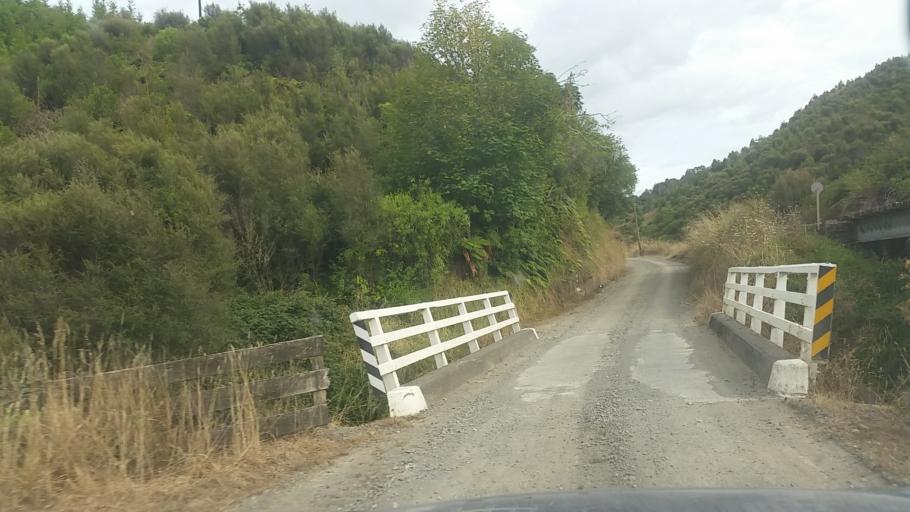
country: NZ
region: Taranaki
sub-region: New Plymouth District
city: Waitara
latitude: -39.1423
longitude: 174.7204
